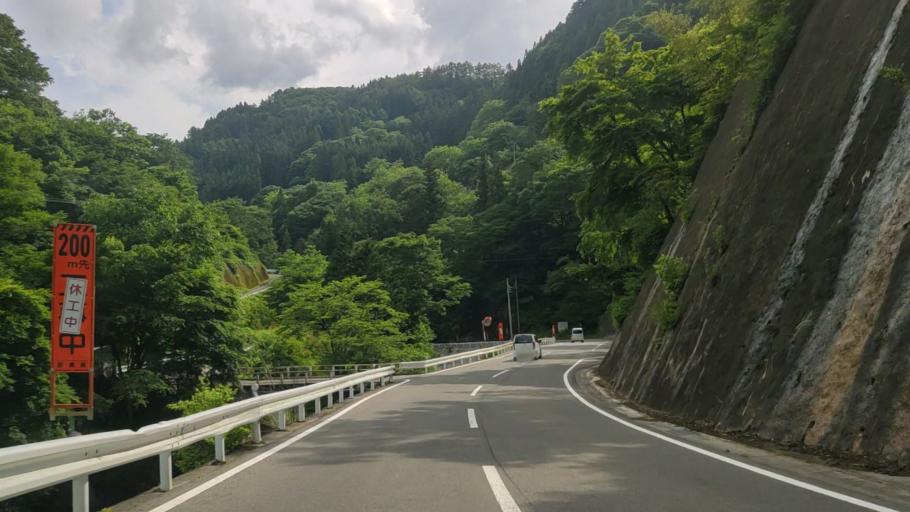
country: JP
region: Gunma
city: Tomioka
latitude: 36.1079
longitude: 138.7176
